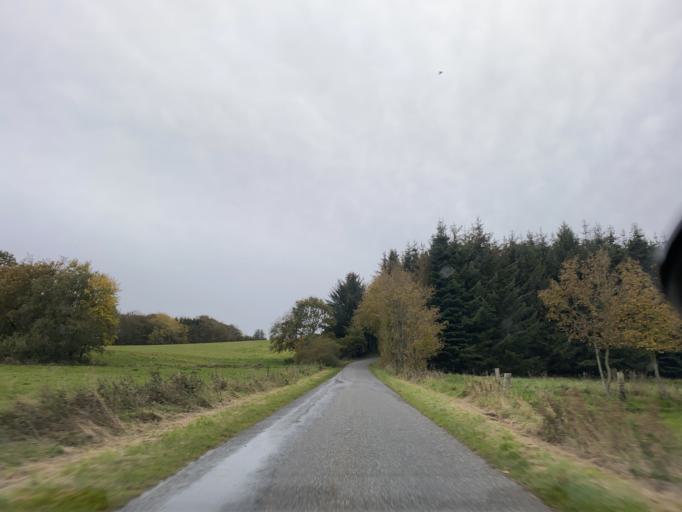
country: DK
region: Central Jutland
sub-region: Favrskov Kommune
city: Hammel
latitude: 56.1967
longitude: 9.7777
